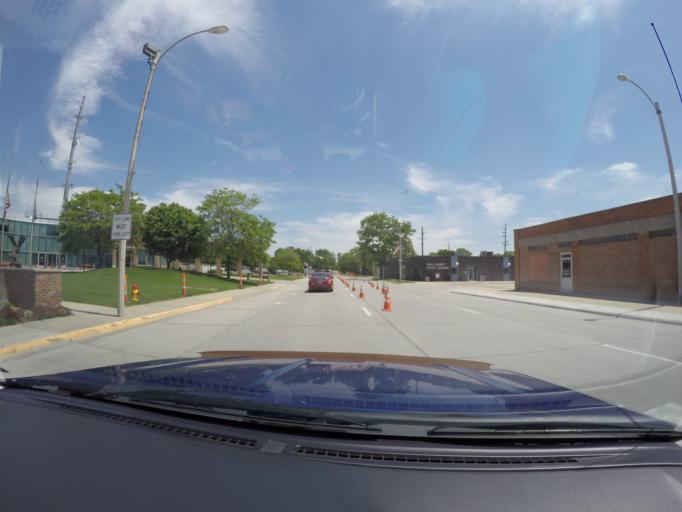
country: US
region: Nebraska
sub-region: Hall County
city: Grand Island
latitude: 40.9242
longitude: -98.3387
